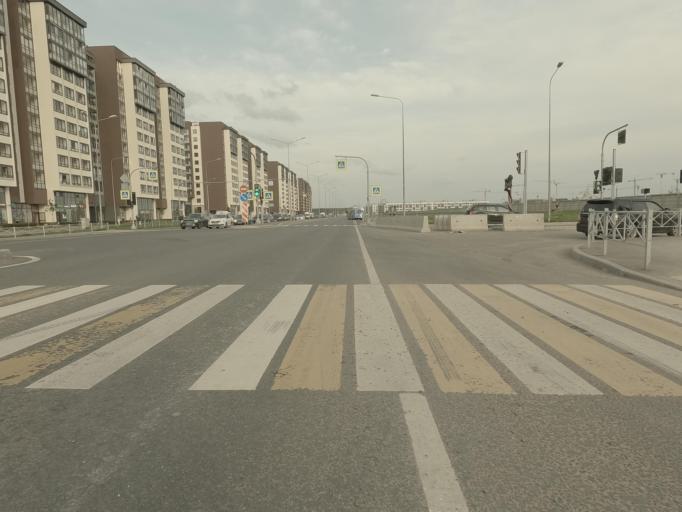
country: RU
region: St.-Petersburg
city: Sosnovaya Polyana
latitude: 59.8380
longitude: 30.1025
